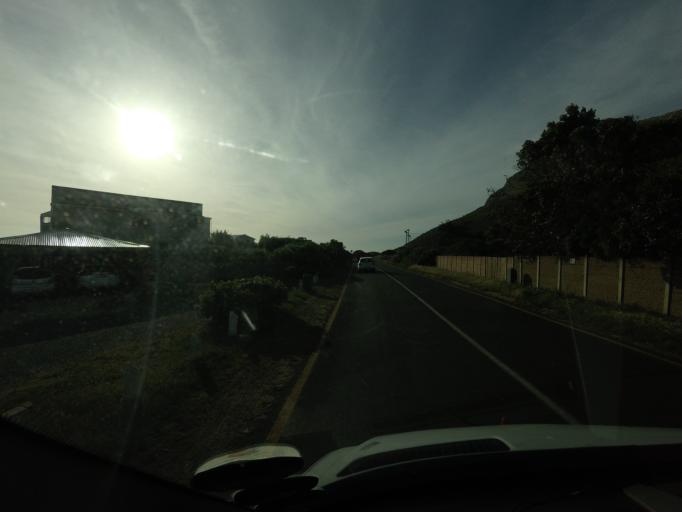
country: ZA
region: Western Cape
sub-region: City of Cape Town
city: Bergvliet
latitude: -34.1964
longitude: 18.3741
